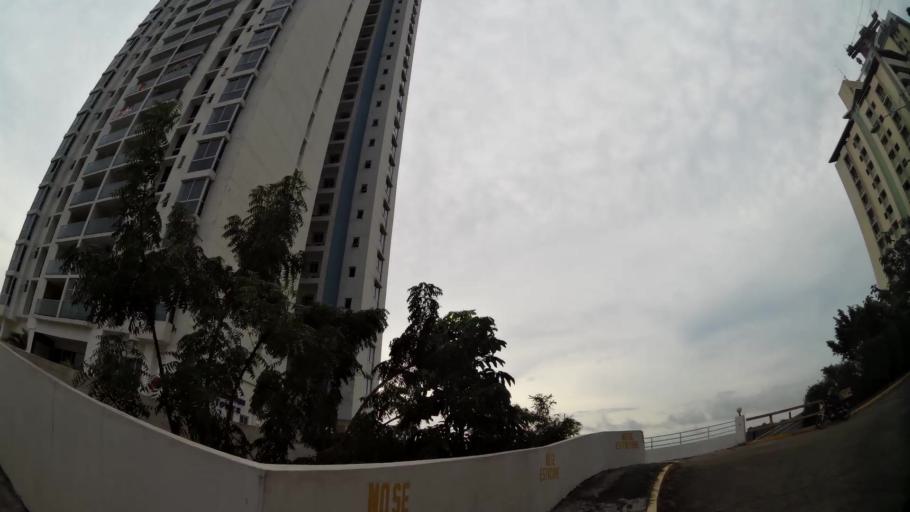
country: PA
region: Panama
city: Panama
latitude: 9.0133
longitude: -79.5337
